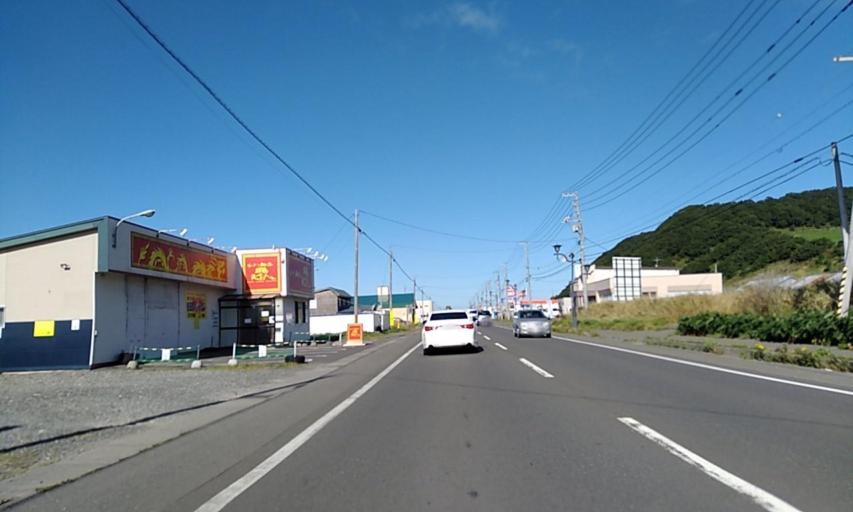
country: JP
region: Hokkaido
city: Shizunai-furukawacho
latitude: 42.3420
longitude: 142.3435
